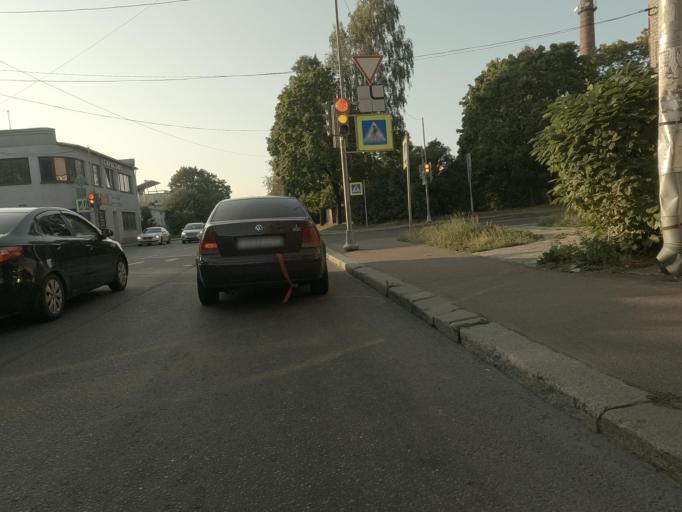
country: RU
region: Leningrad
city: Vyborg
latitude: 60.7118
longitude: 28.7577
